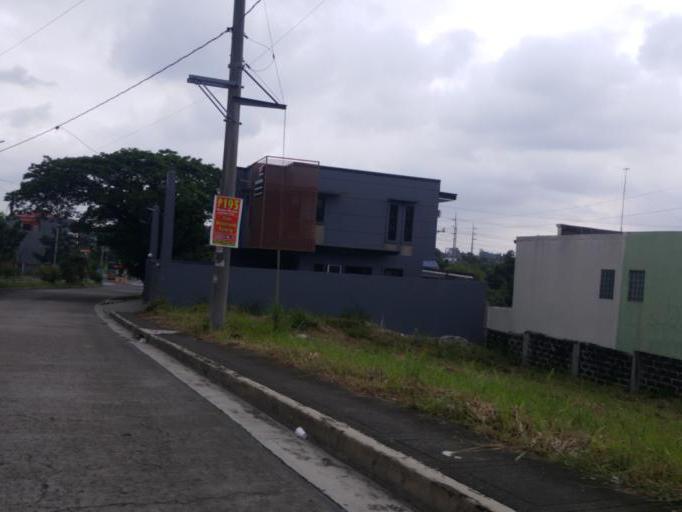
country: PH
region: Calabarzon
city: Bagong Pagasa
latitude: 14.7152
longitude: 121.0207
